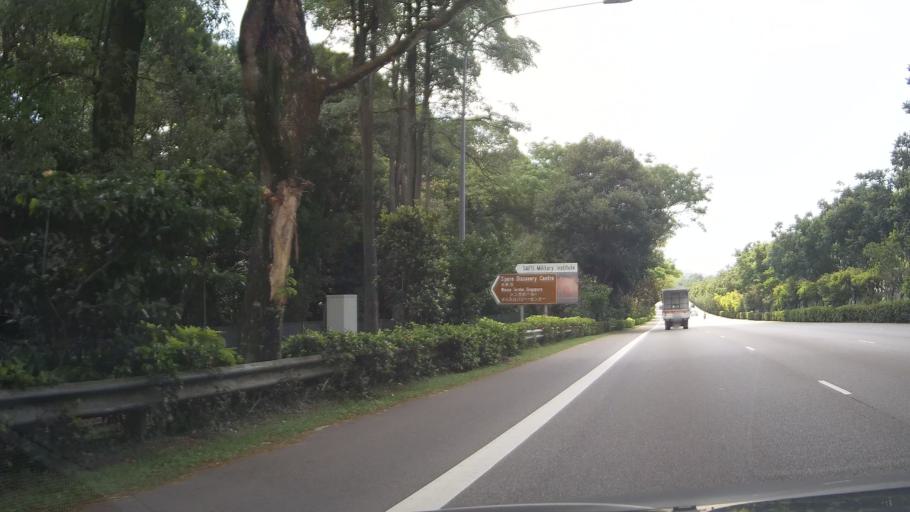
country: MY
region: Johor
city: Johor Bahru
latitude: 1.3373
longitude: 103.6773
